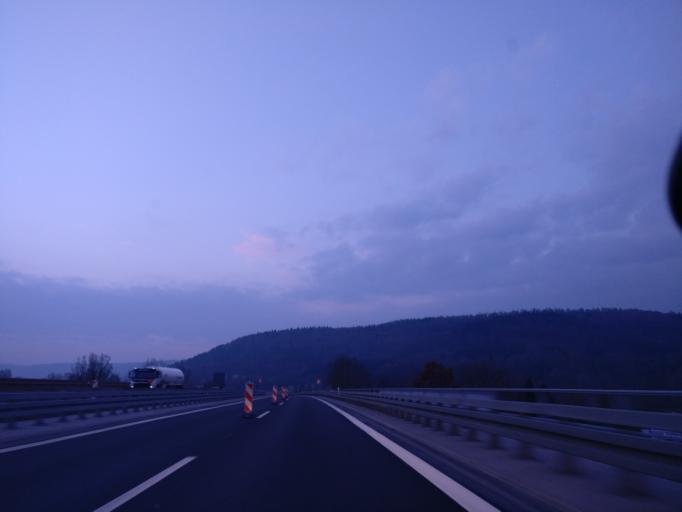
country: DE
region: Baden-Wuerttemberg
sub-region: Regierungsbezirk Stuttgart
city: Urbach
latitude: 48.8059
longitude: 9.5719
